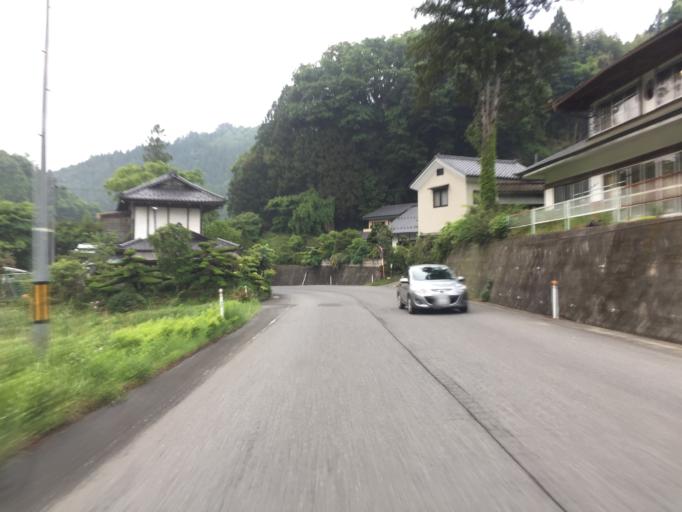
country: JP
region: Fukushima
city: Ishikawa
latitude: 37.1523
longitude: 140.4960
